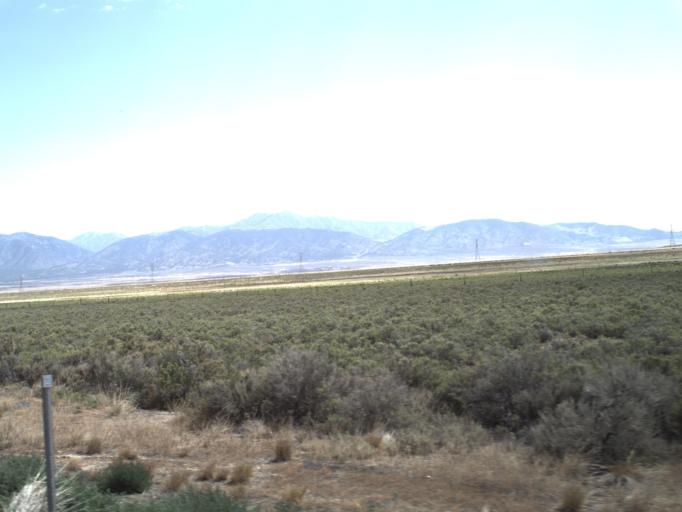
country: US
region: Utah
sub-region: Tooele County
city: Tooele
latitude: 40.2246
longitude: -112.4045
